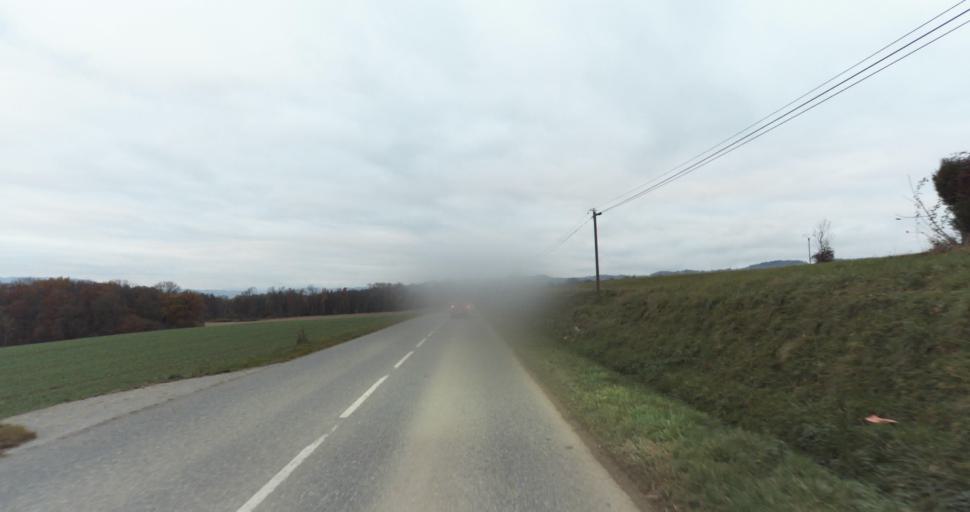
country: FR
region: Rhone-Alpes
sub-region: Departement de la Haute-Savoie
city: Saint-Felix
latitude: 45.8144
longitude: 5.9732
